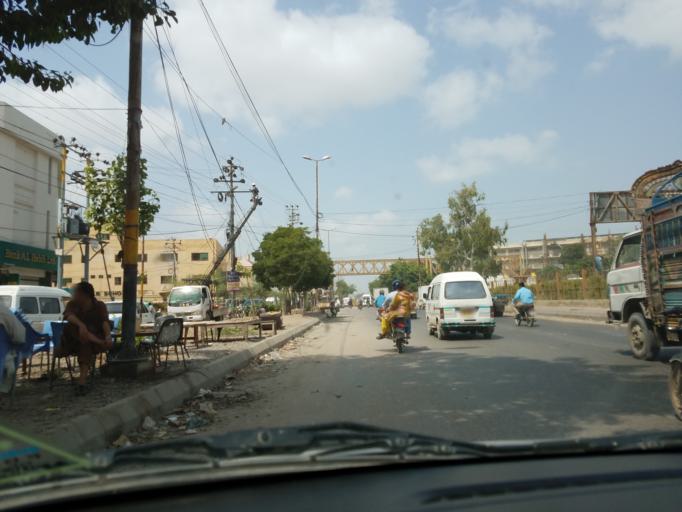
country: PK
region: Sindh
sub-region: Karachi District
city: Karachi
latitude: 24.9490
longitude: 67.0816
